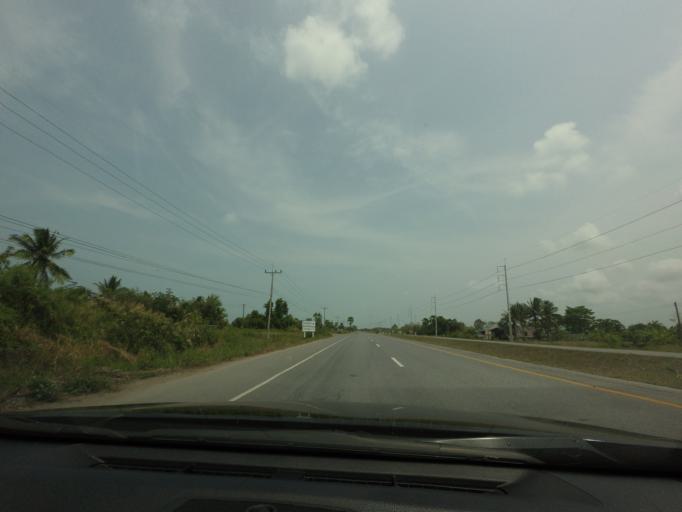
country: TH
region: Nakhon Si Thammarat
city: Hua Sai
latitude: 8.0045
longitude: 100.3021
